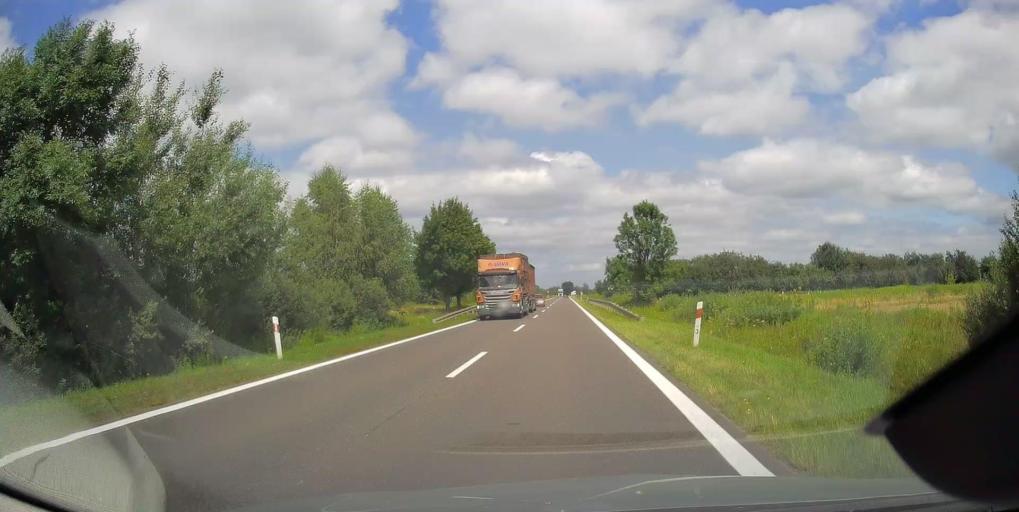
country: PL
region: Subcarpathian Voivodeship
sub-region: Powiat tarnobrzeski
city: Baranow Sandomierski
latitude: 50.4972
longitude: 21.5706
